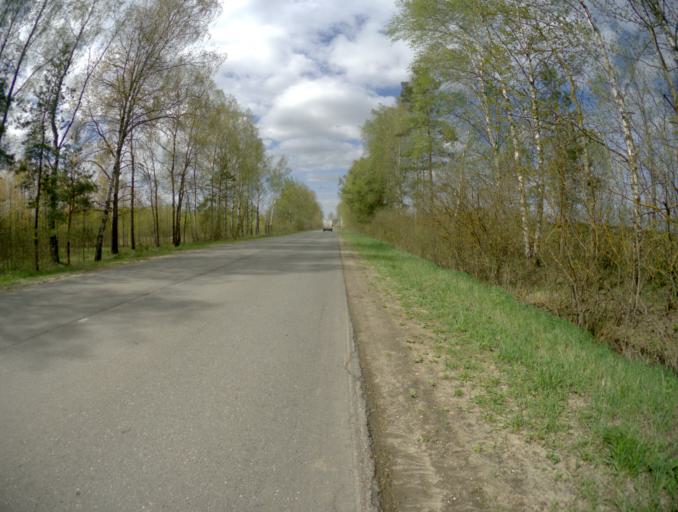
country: RU
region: Vladimir
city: Golovino
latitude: 55.9557
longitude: 40.4555
